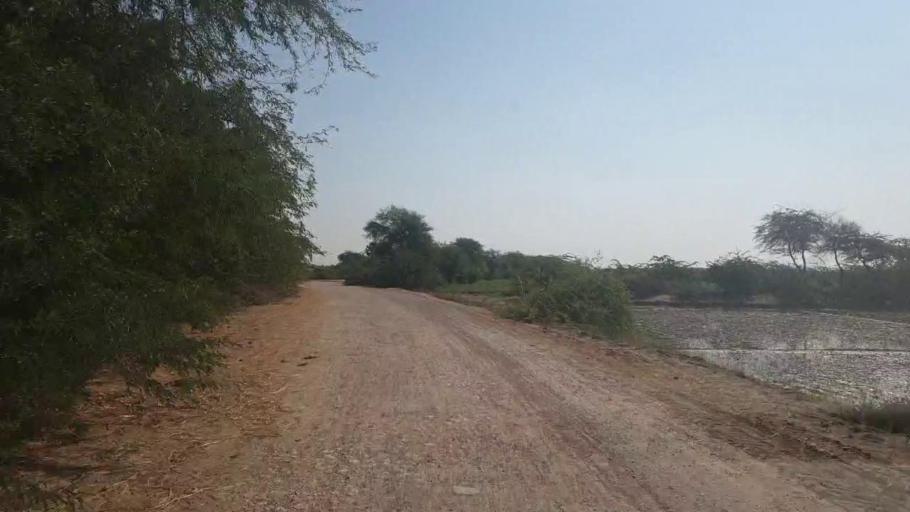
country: PK
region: Sindh
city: Badin
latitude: 24.5992
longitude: 68.8535
